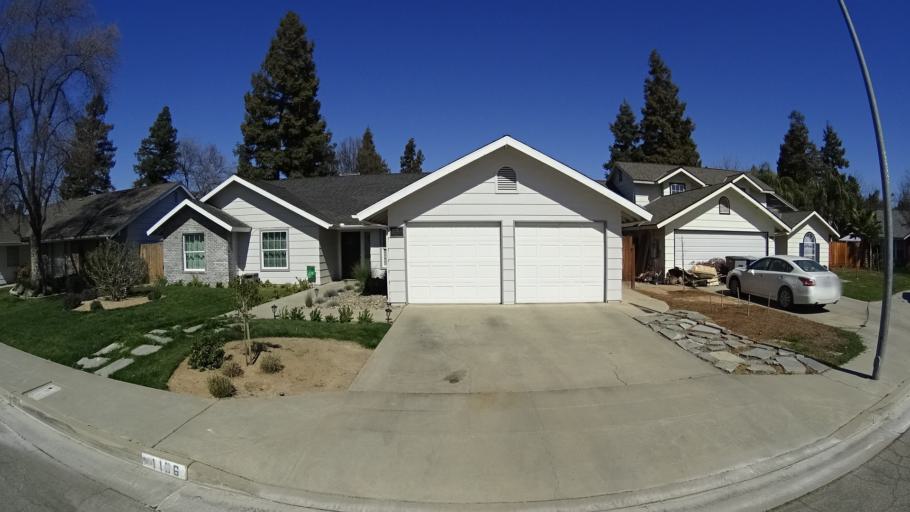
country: US
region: California
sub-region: Fresno County
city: Clovis
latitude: 36.8480
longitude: -119.7621
